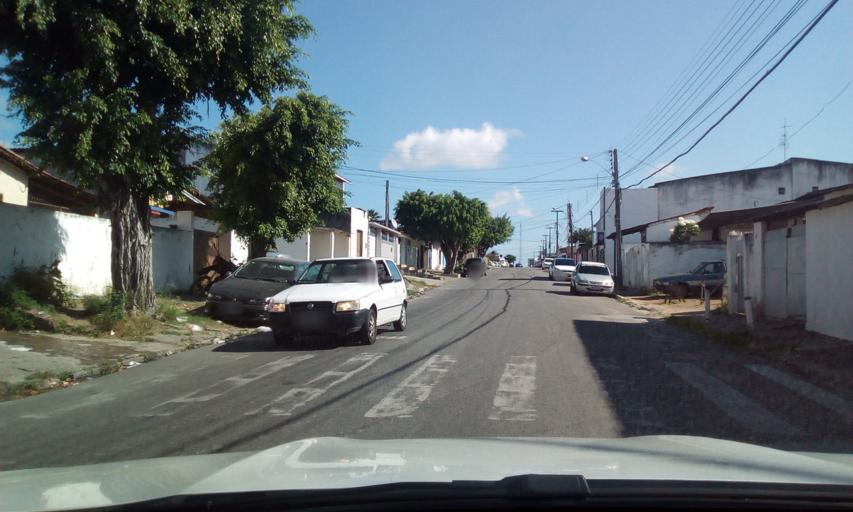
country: BR
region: Paraiba
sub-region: Joao Pessoa
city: Joao Pessoa
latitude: -7.1028
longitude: -34.8631
